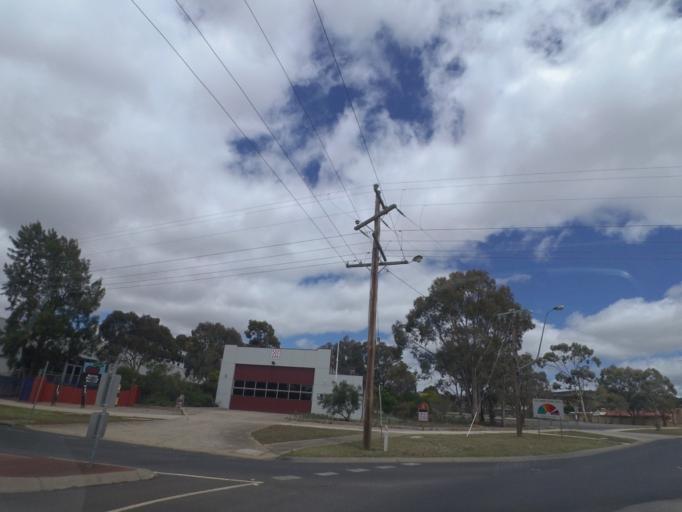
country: AU
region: Victoria
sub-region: Moorabool
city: Bacchus Marsh
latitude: -37.6540
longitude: 144.4378
